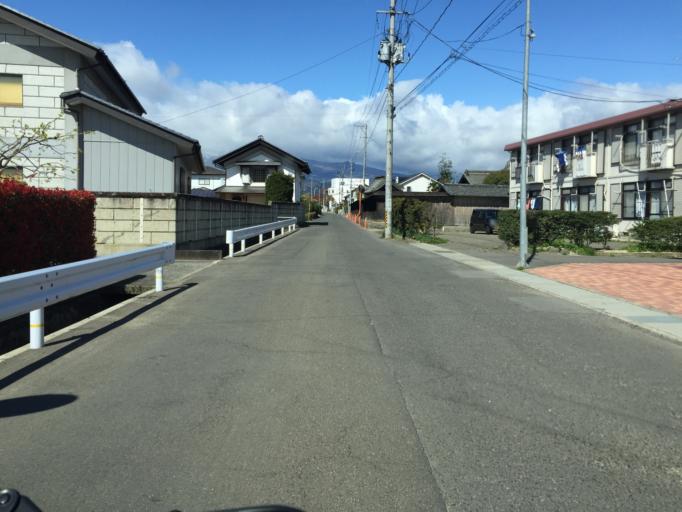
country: JP
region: Fukushima
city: Fukushima-shi
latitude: 37.7343
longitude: 140.4275
